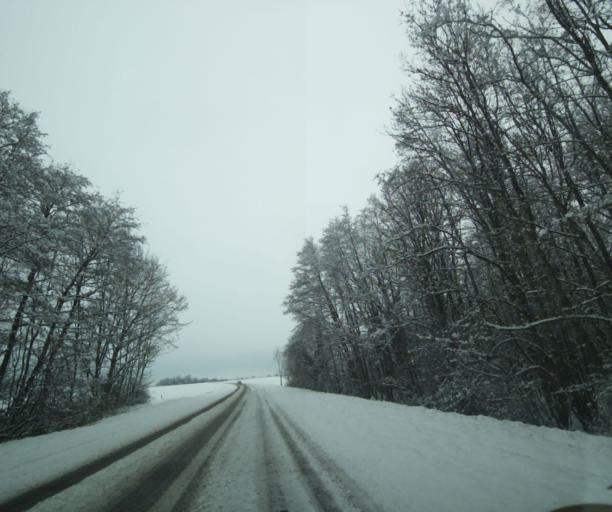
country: FR
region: Champagne-Ardenne
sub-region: Departement de la Haute-Marne
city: Montier-en-Der
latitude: 48.5249
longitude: 4.8003
